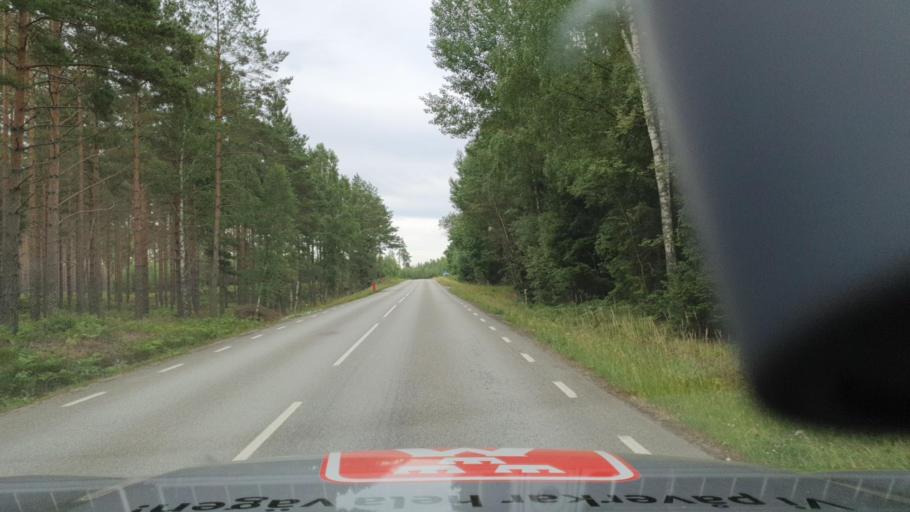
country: SE
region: Kalmar
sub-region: Nybro Kommun
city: Nybro
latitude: 56.6665
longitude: 15.9964
